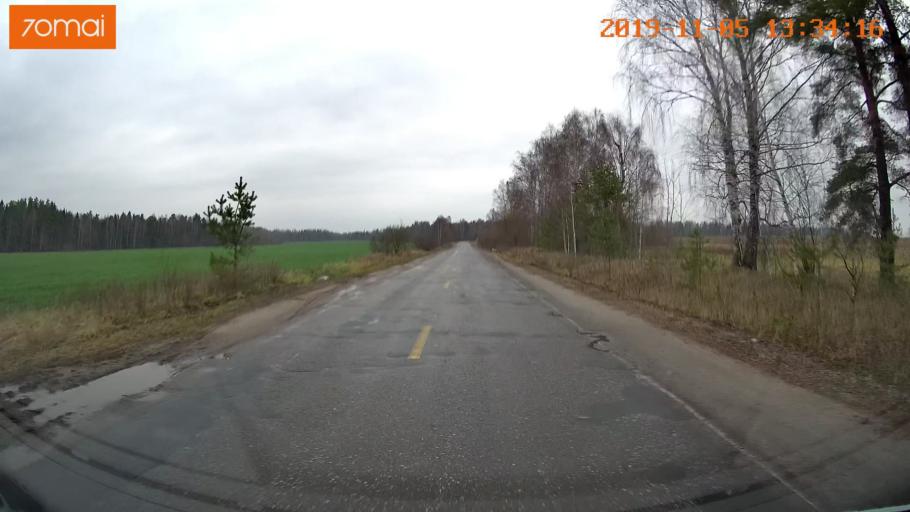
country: RU
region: Ivanovo
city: Shuya
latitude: 56.8992
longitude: 41.3900
